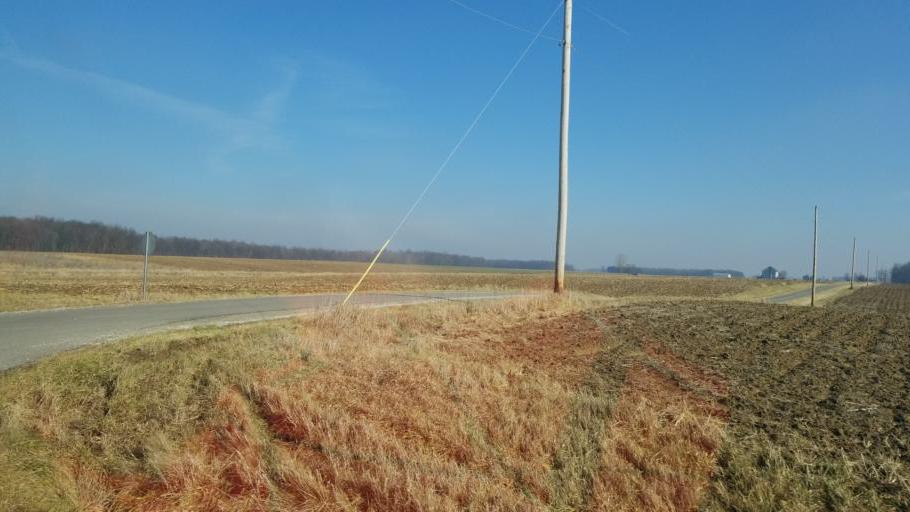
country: US
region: Ohio
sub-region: Seneca County
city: Tiffin
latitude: 40.9723
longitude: -83.0743
